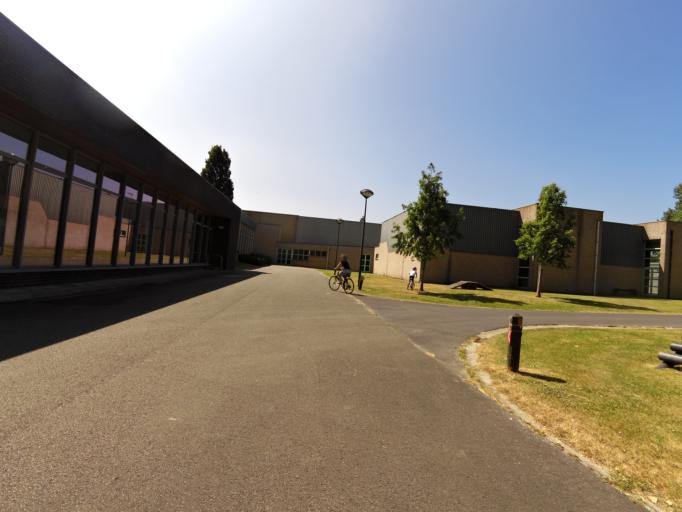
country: BE
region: Flanders
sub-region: Provincie West-Vlaanderen
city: Zedelgem
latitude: 51.1398
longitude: 3.1538
